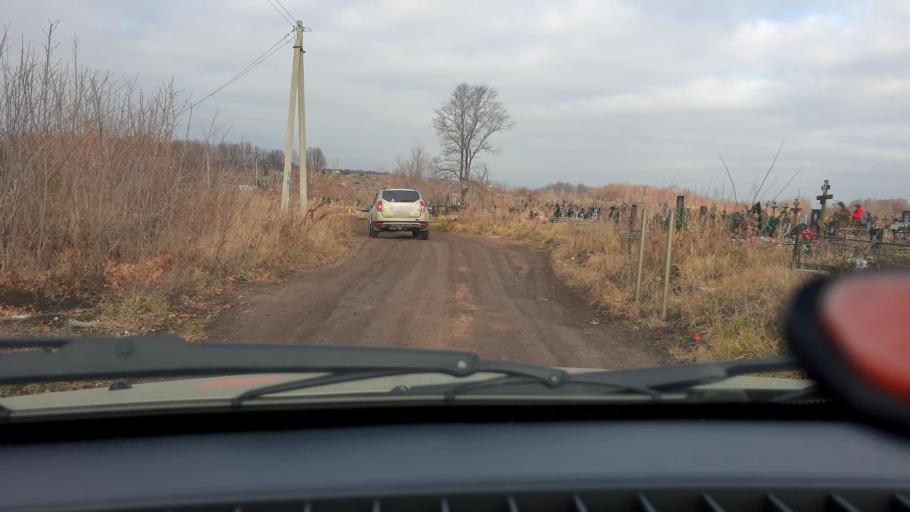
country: RU
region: Bashkortostan
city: Ufa
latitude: 54.8578
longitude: 56.1652
